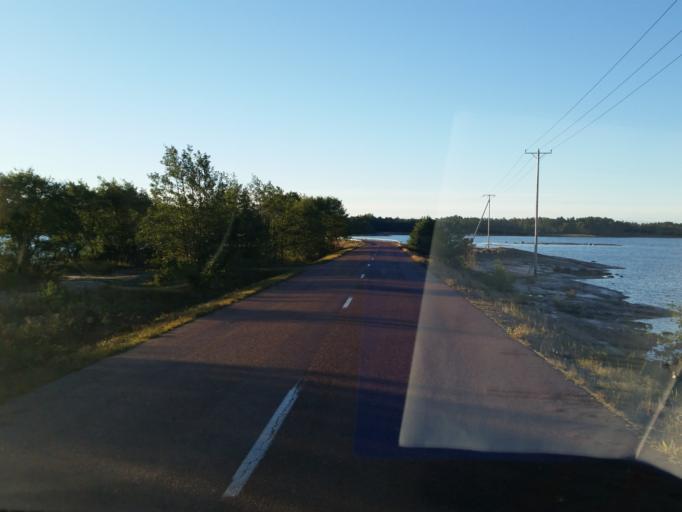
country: AX
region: Alands skaergard
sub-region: Vardoe
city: Vardoe
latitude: 60.3134
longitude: 20.3744
